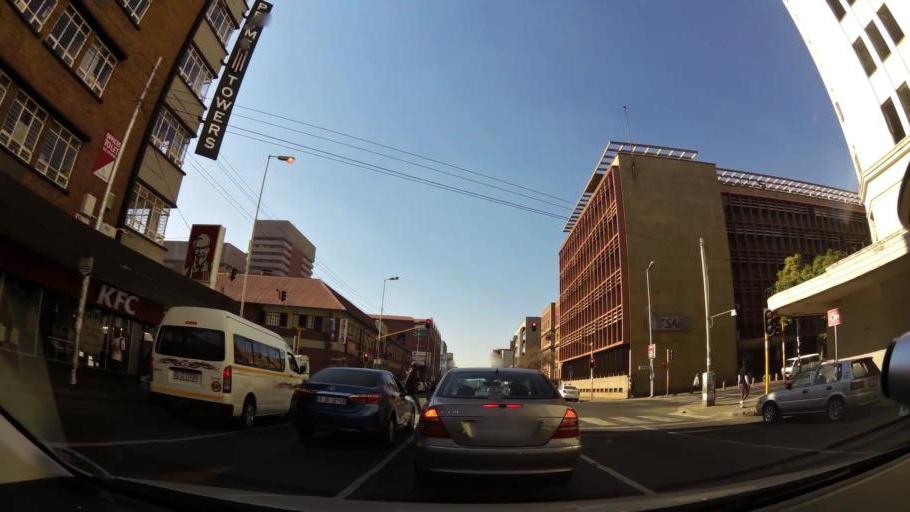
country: ZA
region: Gauteng
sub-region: City of Tshwane Metropolitan Municipality
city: Pretoria
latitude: -25.7489
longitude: 28.1929
